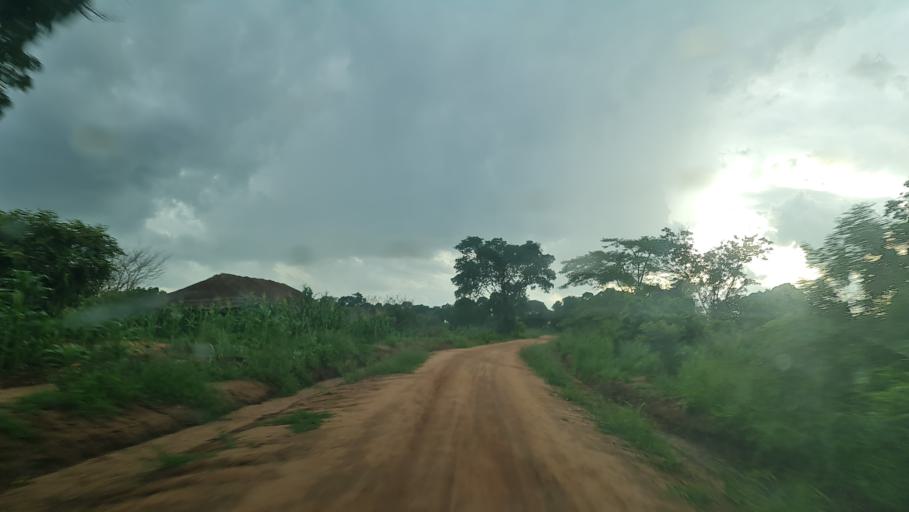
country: MZ
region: Nampula
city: Nacala
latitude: -13.9997
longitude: 40.3606
